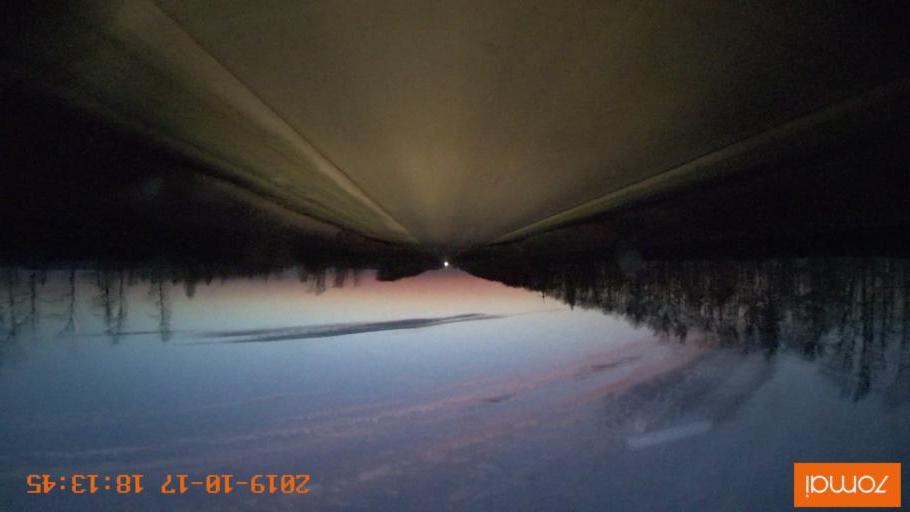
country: RU
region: Tula
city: Kurkino
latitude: 53.4094
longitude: 38.5795
